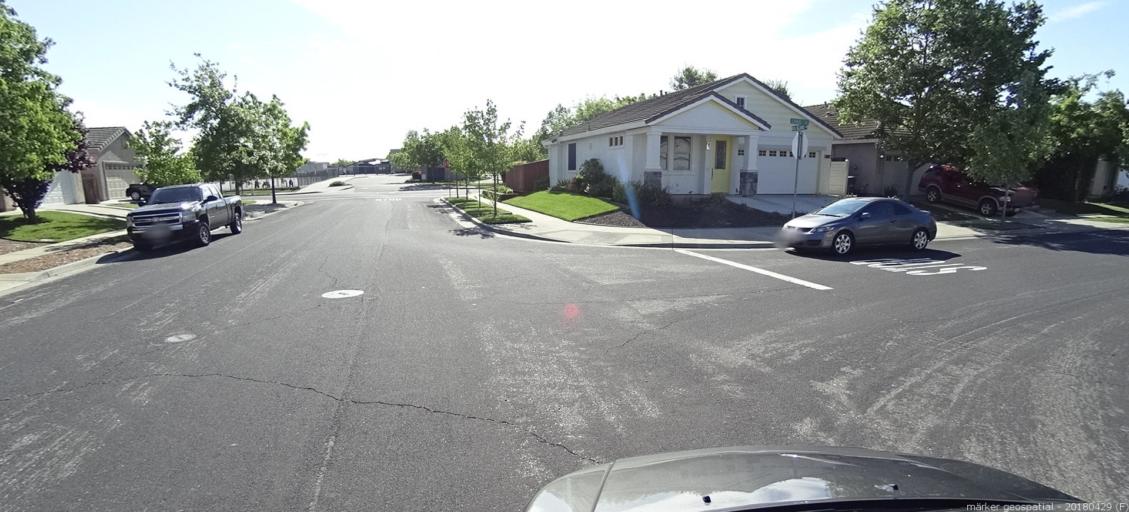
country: US
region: California
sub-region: Yolo County
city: West Sacramento
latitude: 38.5410
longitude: -121.5695
